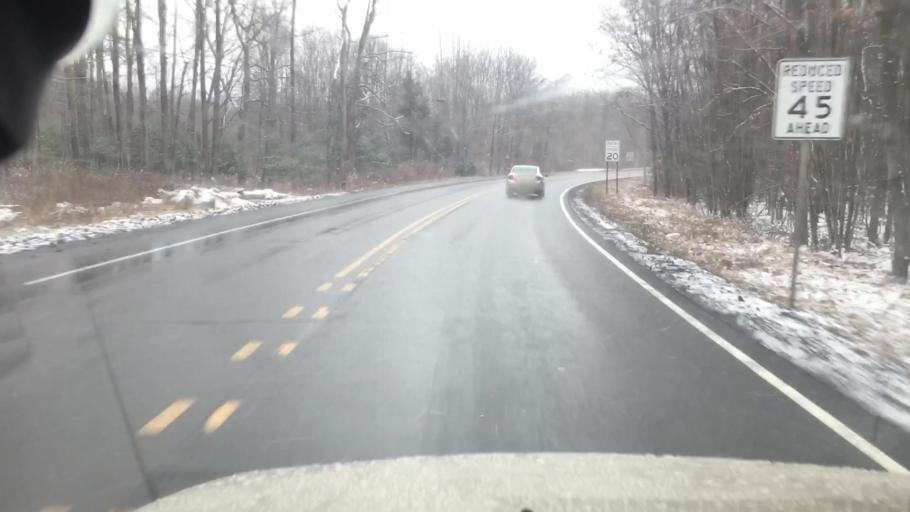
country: US
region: Pennsylvania
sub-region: Luzerne County
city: Conyngham
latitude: 41.0303
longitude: -76.0804
